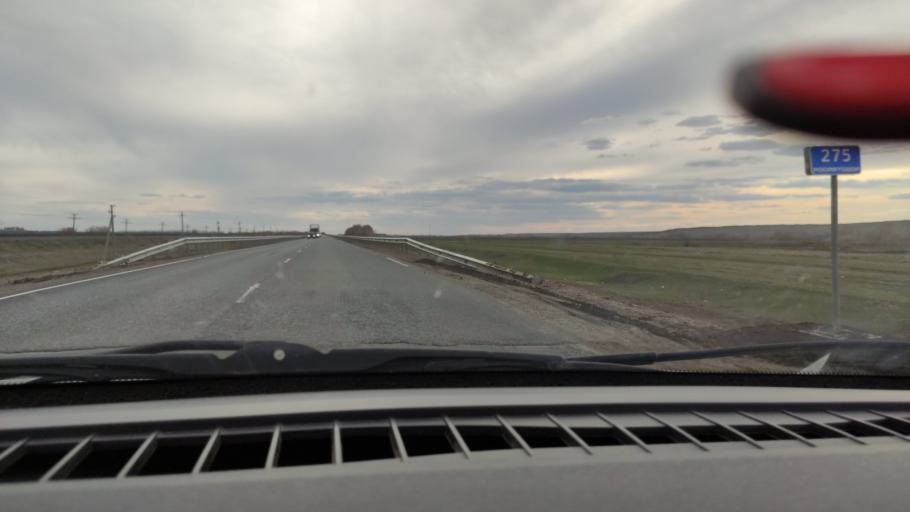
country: RU
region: Bashkortostan
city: Mayachnyy
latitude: 52.4147
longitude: 55.7585
